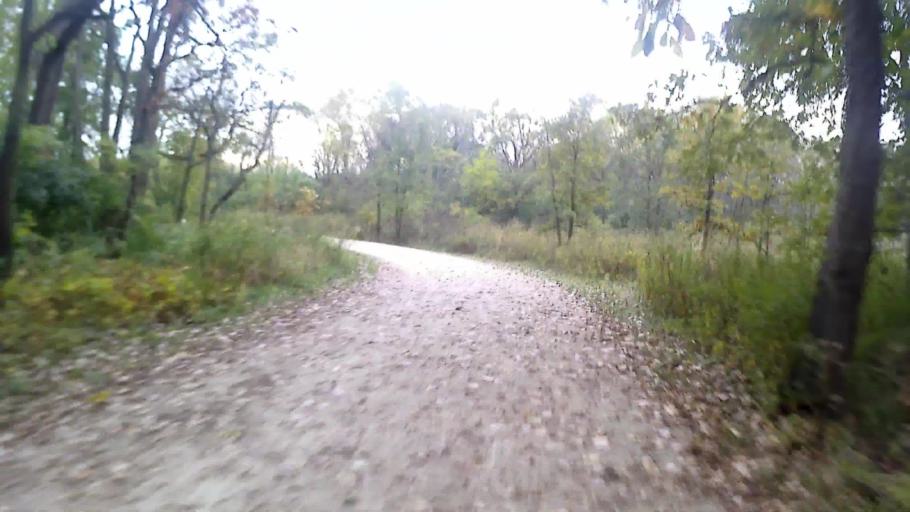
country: US
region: Illinois
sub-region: DuPage County
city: Naperville
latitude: 41.8119
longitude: -88.1402
